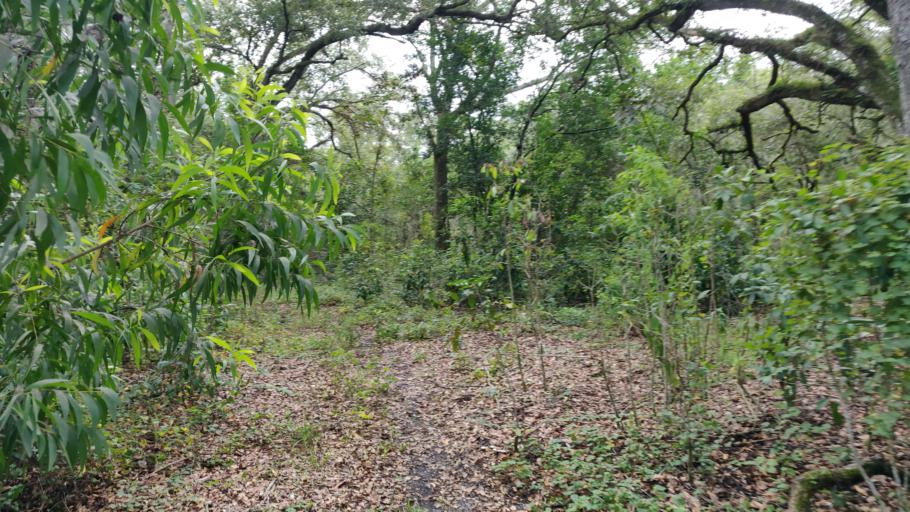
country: US
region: Florida
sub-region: Broward County
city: Cooper City
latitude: 26.0736
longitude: -80.2724
